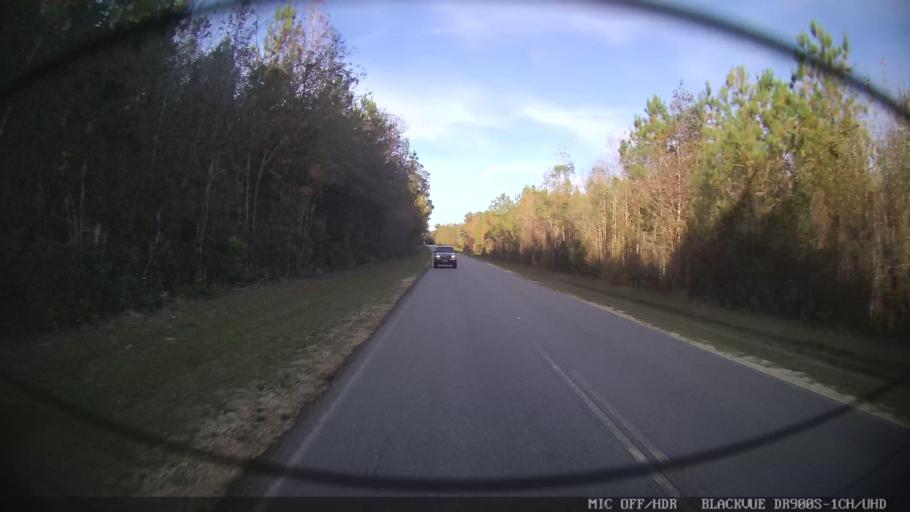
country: US
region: Mississippi
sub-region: Lamar County
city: Purvis
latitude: 31.1543
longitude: -89.3341
